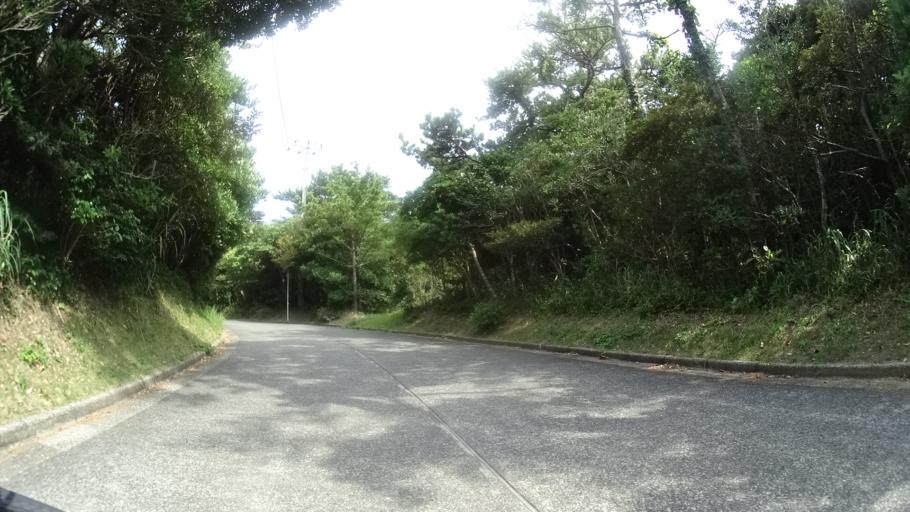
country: JP
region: Shizuoka
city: Shimoda
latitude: 34.3249
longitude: 139.2087
